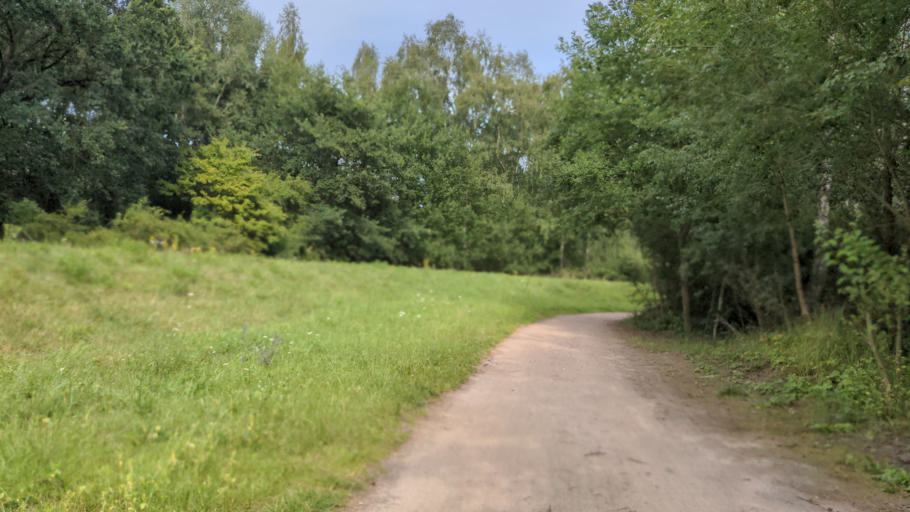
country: DE
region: Mecklenburg-Vorpommern
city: Ostseebad Boltenhagen
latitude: 53.9810
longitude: 11.2424
